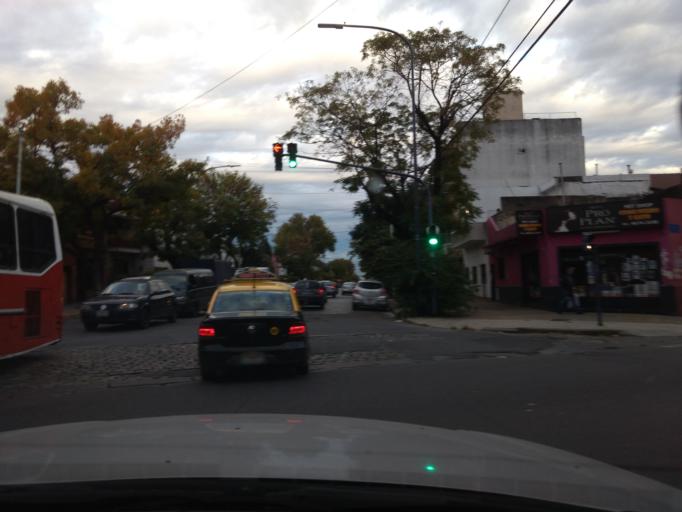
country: AR
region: Buenos Aires F.D.
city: Villa Santa Rita
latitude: -34.6314
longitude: -58.4924
